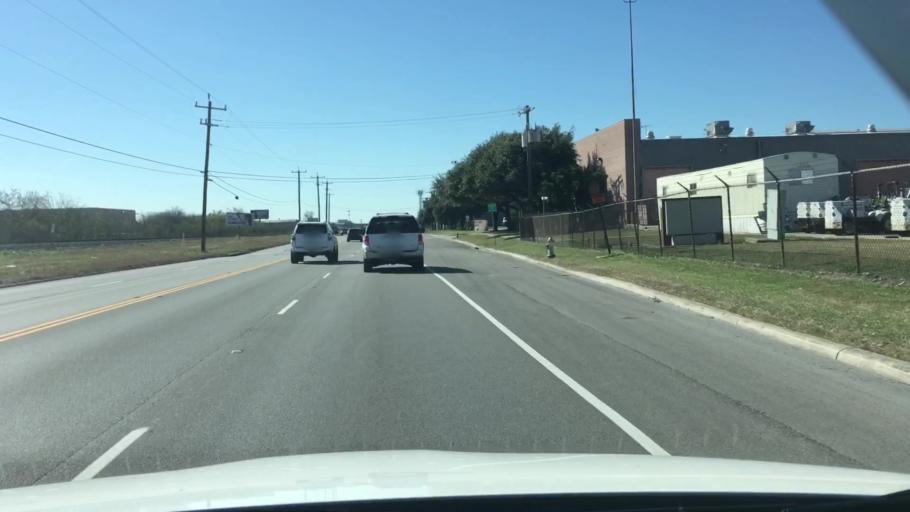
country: US
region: Texas
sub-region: Bexar County
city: Alamo Heights
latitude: 29.5323
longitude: -98.4557
